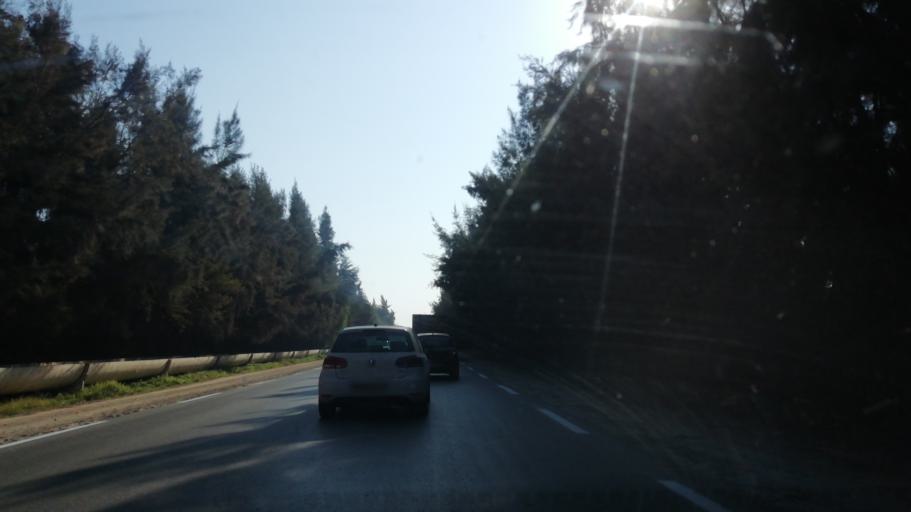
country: DZ
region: Relizane
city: Relizane
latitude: 35.7316
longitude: 0.4717
